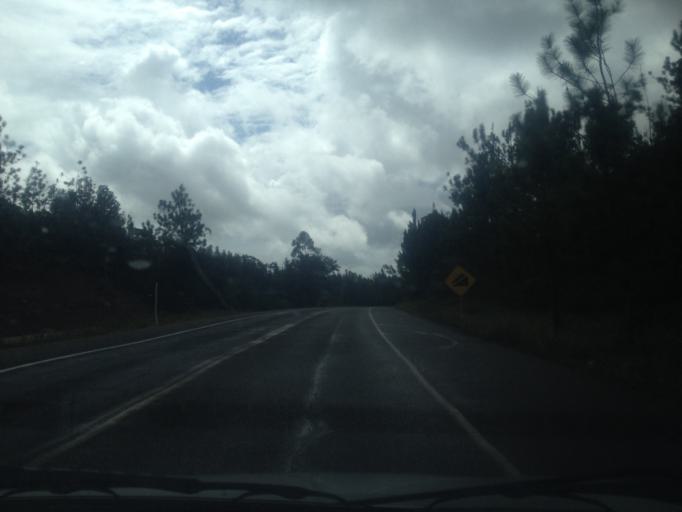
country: BR
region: Bahia
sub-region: Conde
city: Conde
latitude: -12.1048
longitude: -37.7830
